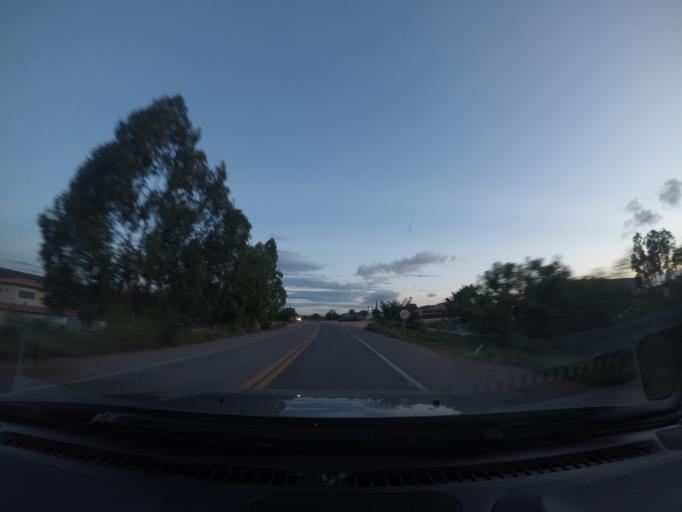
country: BR
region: Bahia
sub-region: Seabra
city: Seabra
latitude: -12.4589
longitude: -41.7490
